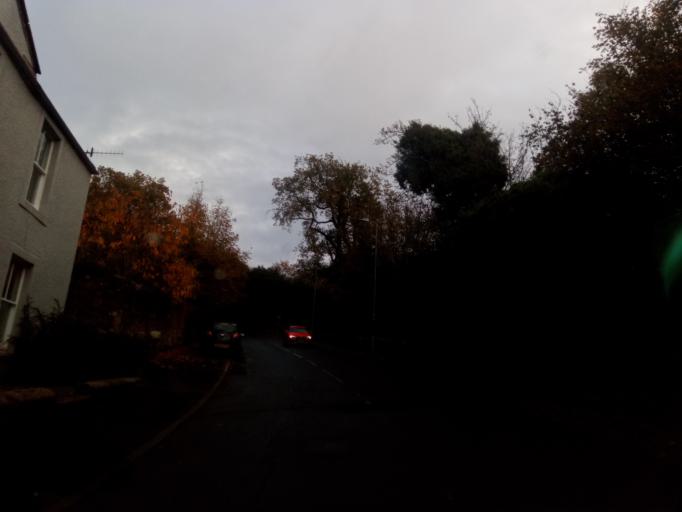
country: GB
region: Scotland
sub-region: The Scottish Borders
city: Eyemouth
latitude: 55.8432
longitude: -2.1210
